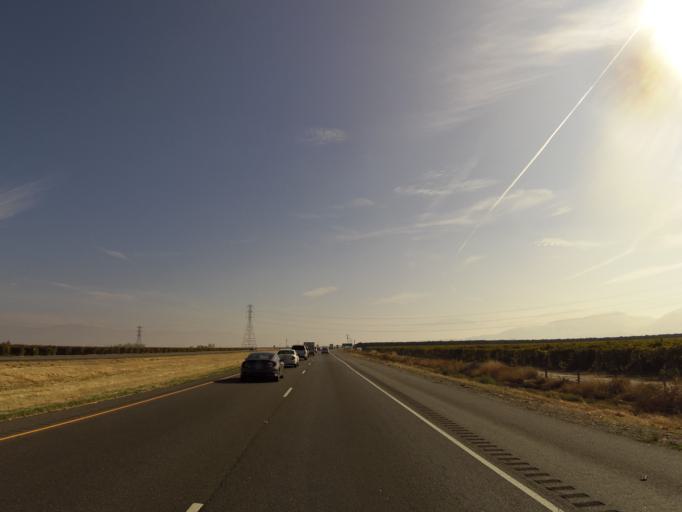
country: US
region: California
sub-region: Kern County
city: Weedpatch
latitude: 35.0513
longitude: -118.9907
